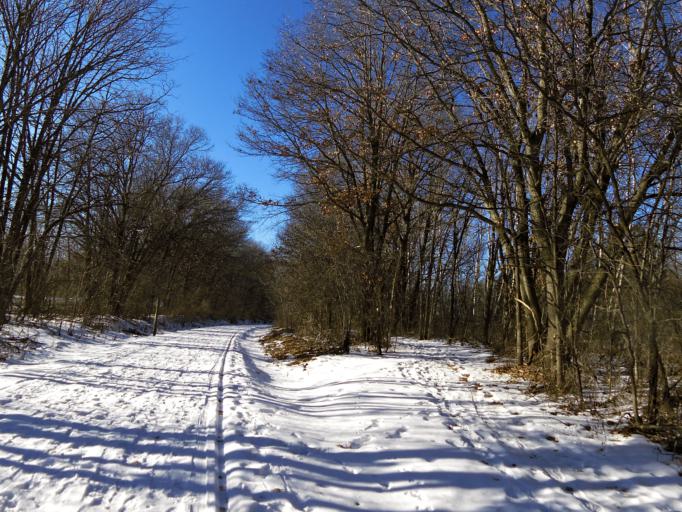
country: US
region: Minnesota
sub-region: Washington County
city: Grant
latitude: 45.0738
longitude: -92.8731
